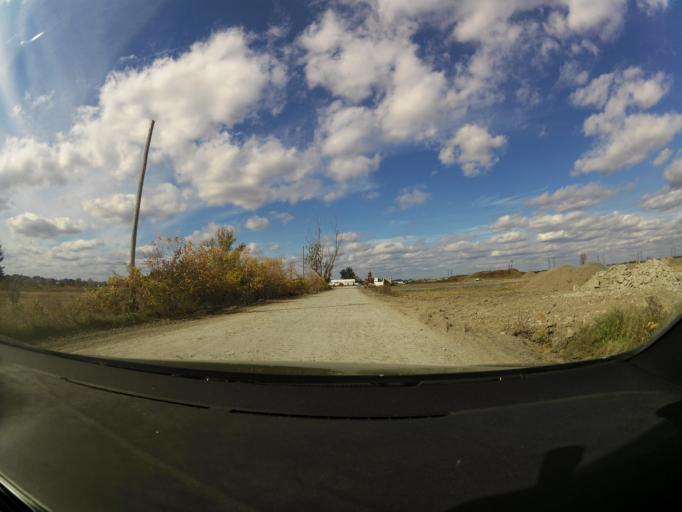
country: CA
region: Ontario
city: Bells Corners
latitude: 45.2685
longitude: -75.8789
